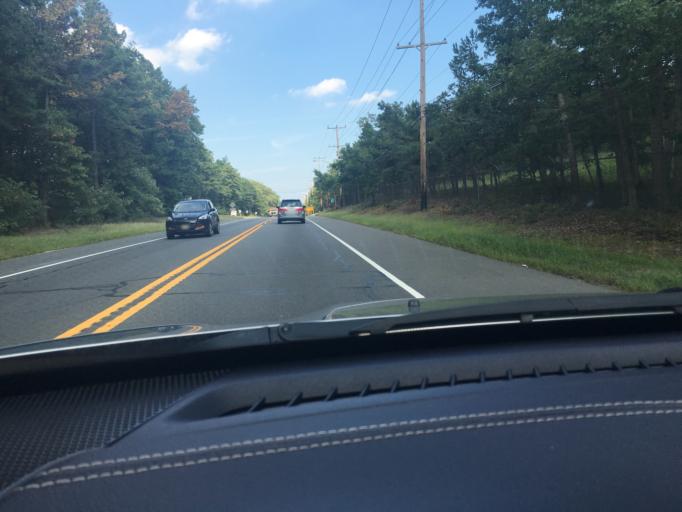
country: US
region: New Jersey
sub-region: Ocean County
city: Leisure Village West-Pine Lake Park
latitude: 40.0256
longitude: -74.2653
